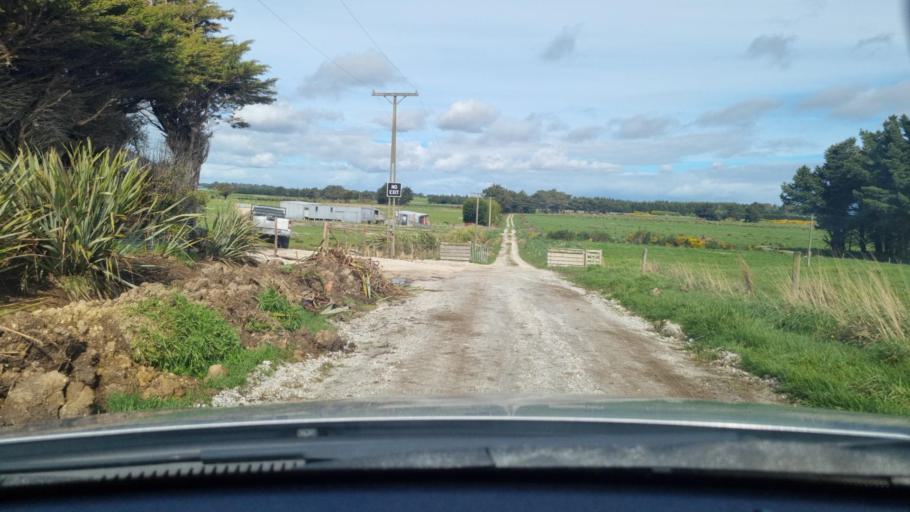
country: NZ
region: Southland
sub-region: Invercargill City
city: Invercargill
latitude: -46.4585
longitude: 168.3885
